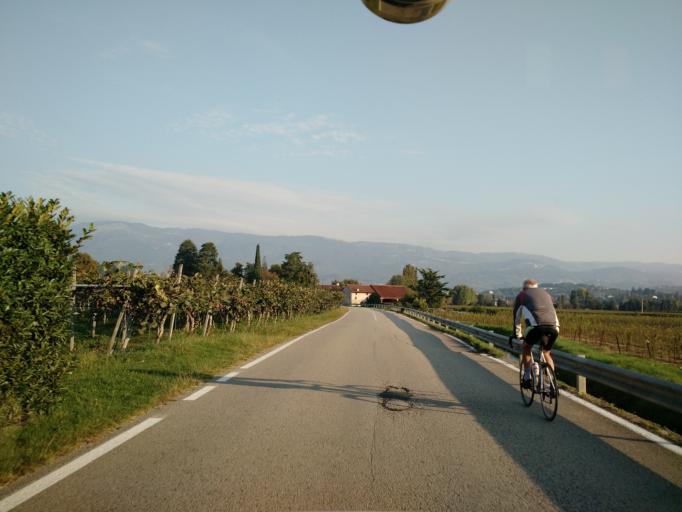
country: IT
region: Veneto
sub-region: Provincia di Vicenza
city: Sarcedo
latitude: 45.6959
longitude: 11.5393
